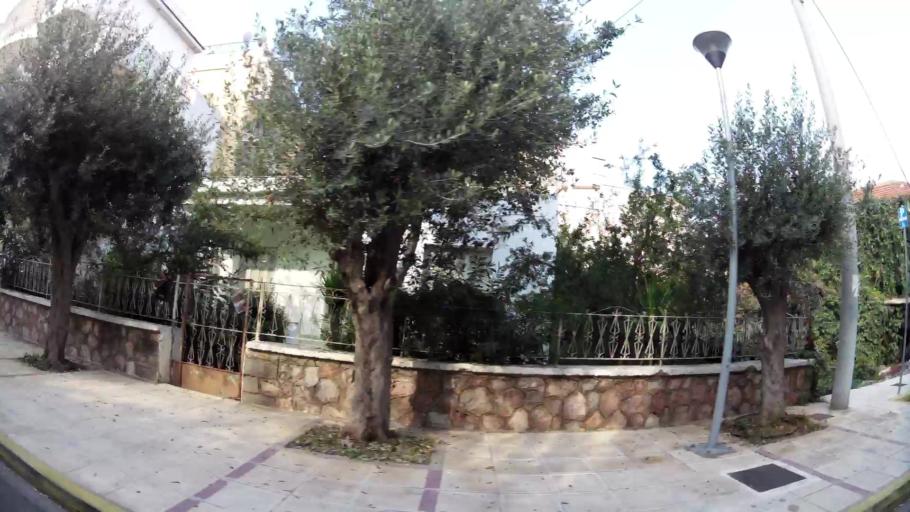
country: GR
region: Attica
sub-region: Nomarchia Athinas
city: Kallithea
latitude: 37.9561
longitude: 23.6893
